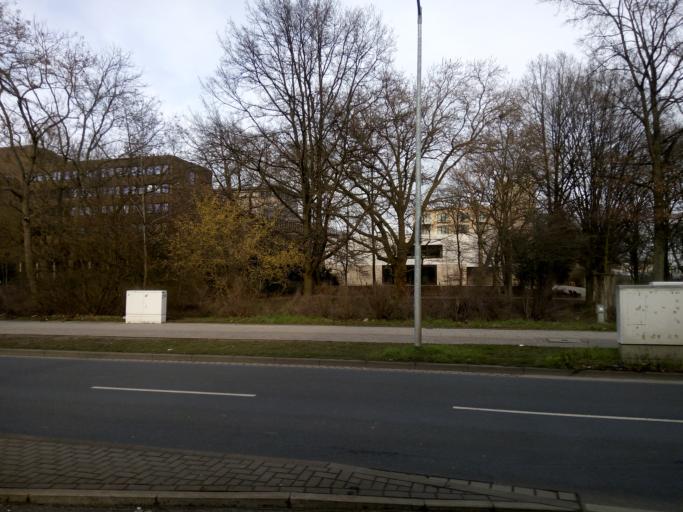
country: DE
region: Lower Saxony
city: Laatzen
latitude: 52.3324
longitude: 9.7735
